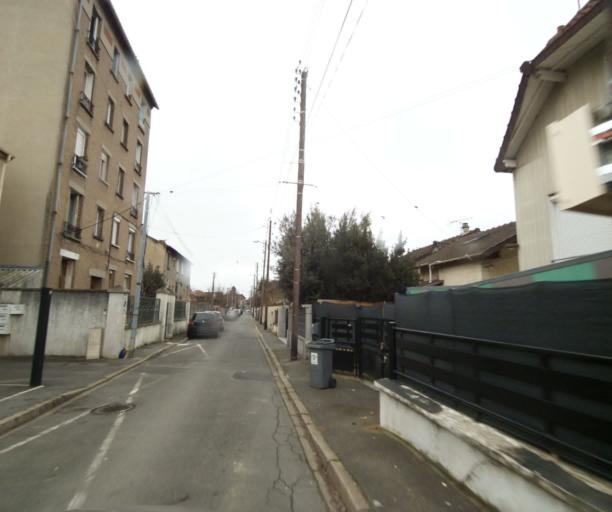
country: FR
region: Ile-de-France
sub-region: Departement du Val-de-Marne
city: Villeneuve-Saint-Georges
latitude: 48.7289
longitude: 2.4395
